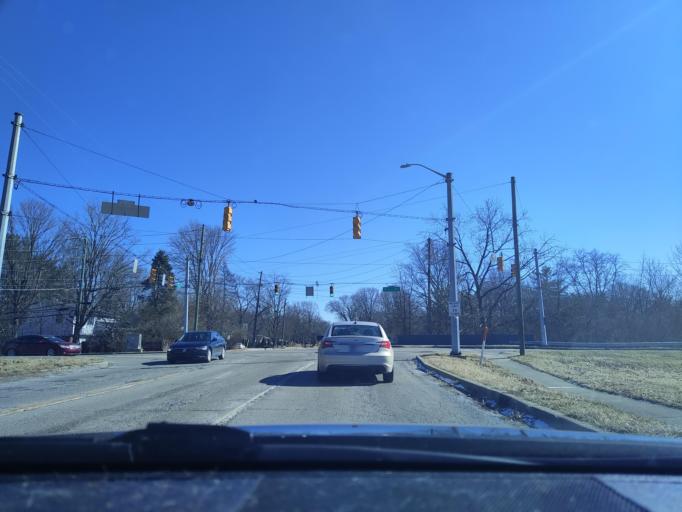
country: US
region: Indiana
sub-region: Marion County
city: Meridian Hills
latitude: 39.8975
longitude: -86.1844
